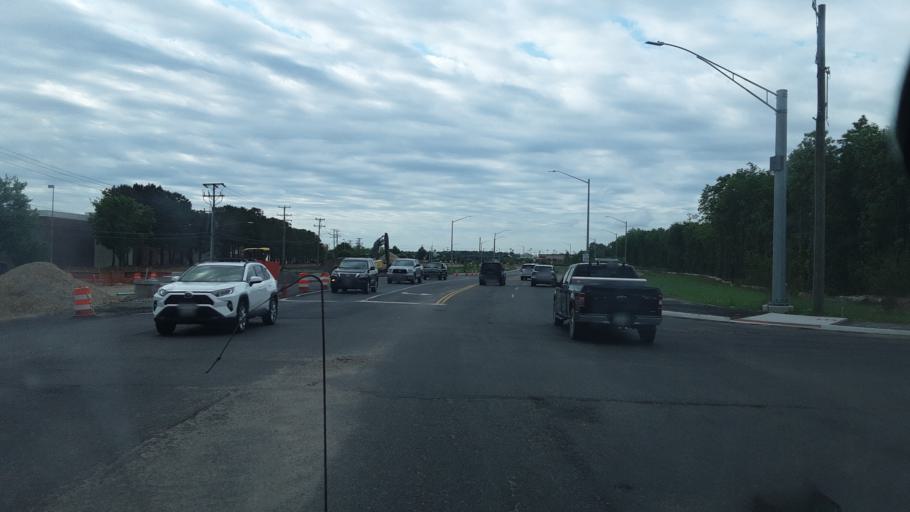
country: US
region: Virginia
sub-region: City of Virginia Beach
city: Virginia Beach
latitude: 36.7564
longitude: -76.0119
